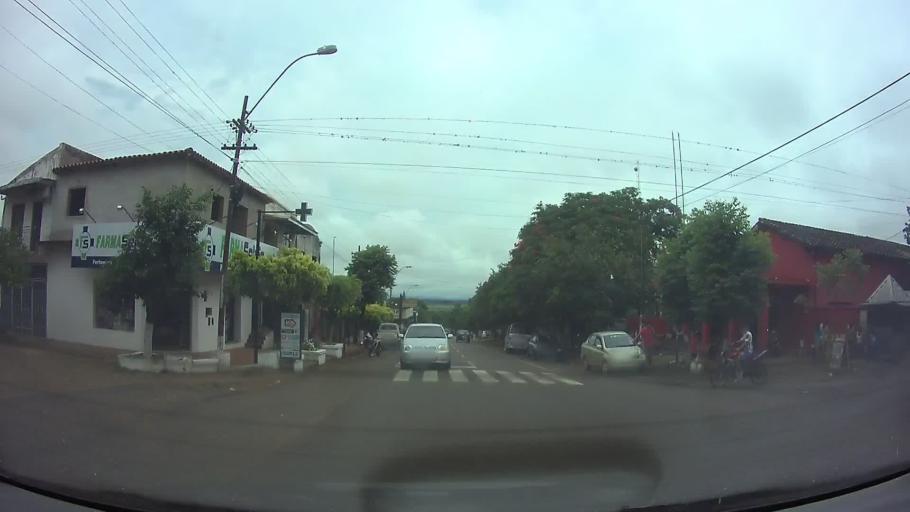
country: PY
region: Paraguari
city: Acahay
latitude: -25.9120
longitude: -57.1149
